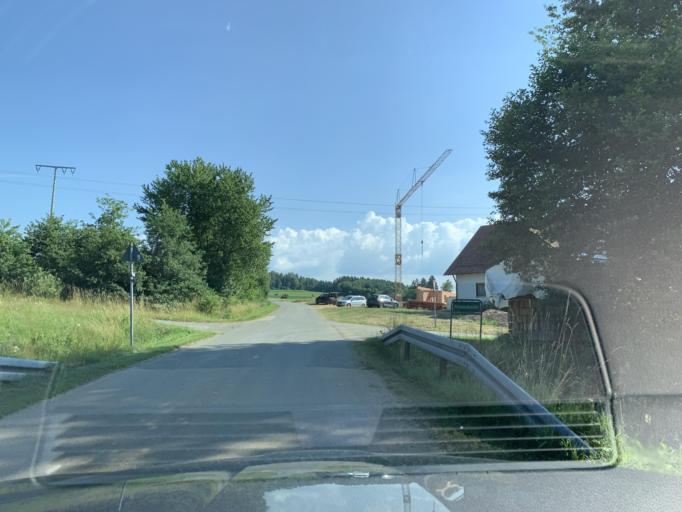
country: DE
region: Bavaria
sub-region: Upper Palatinate
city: Dieterskirchen
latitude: 49.4162
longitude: 12.4293
